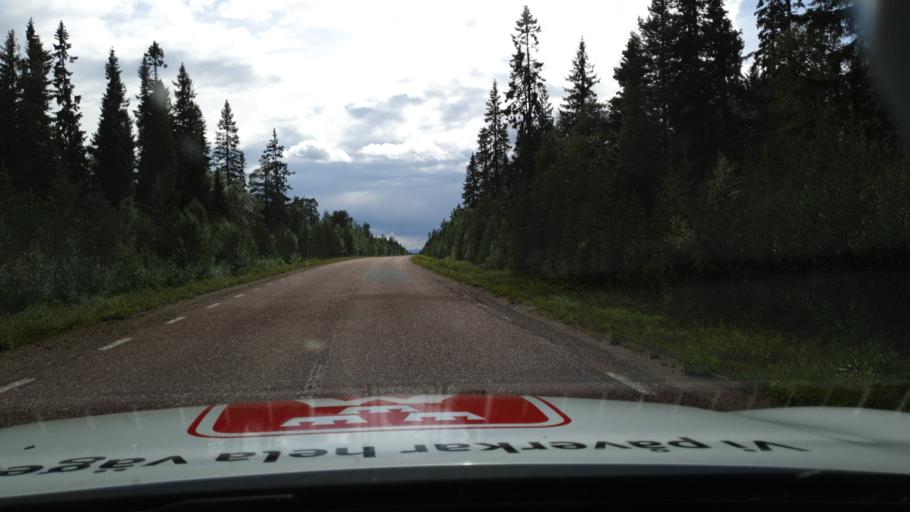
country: SE
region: Dalarna
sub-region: Alvdalens Kommun
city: AElvdalen
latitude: 61.7675
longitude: 13.4784
